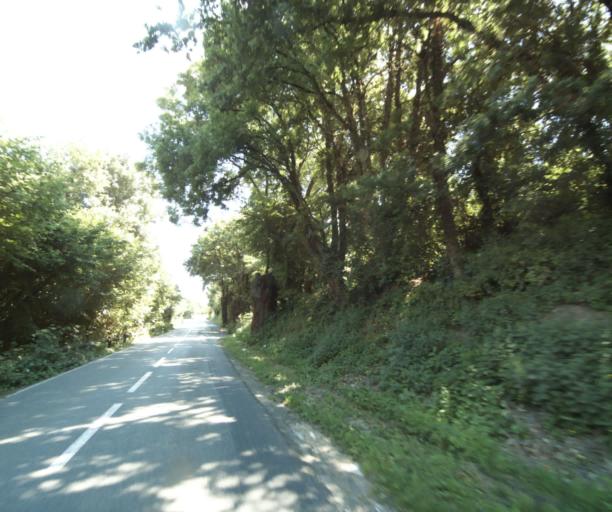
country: FR
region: Pays de la Loire
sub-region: Departement de la Mayenne
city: Change
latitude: 48.0870
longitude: -0.7771
